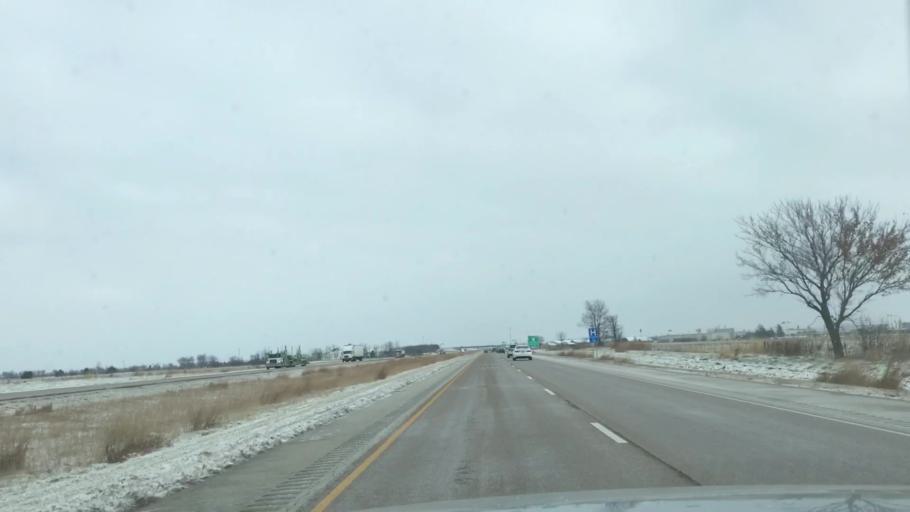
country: US
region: Illinois
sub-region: Montgomery County
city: Litchfield
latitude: 39.1630
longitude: -89.6891
